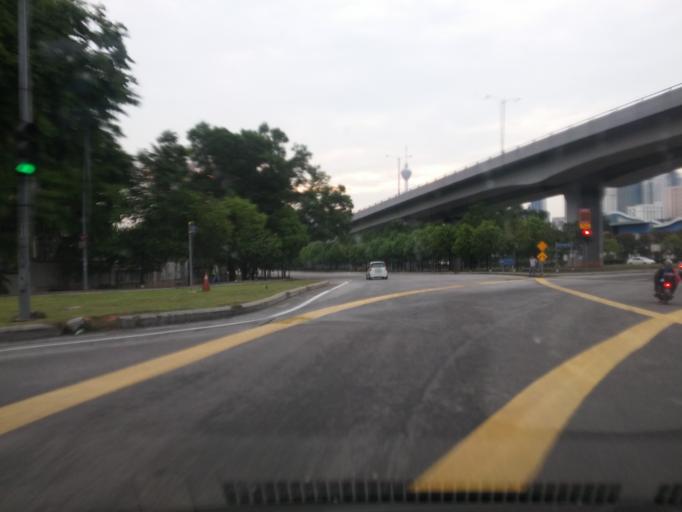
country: MY
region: Kuala Lumpur
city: Kuala Lumpur
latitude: 3.1386
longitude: 101.7197
